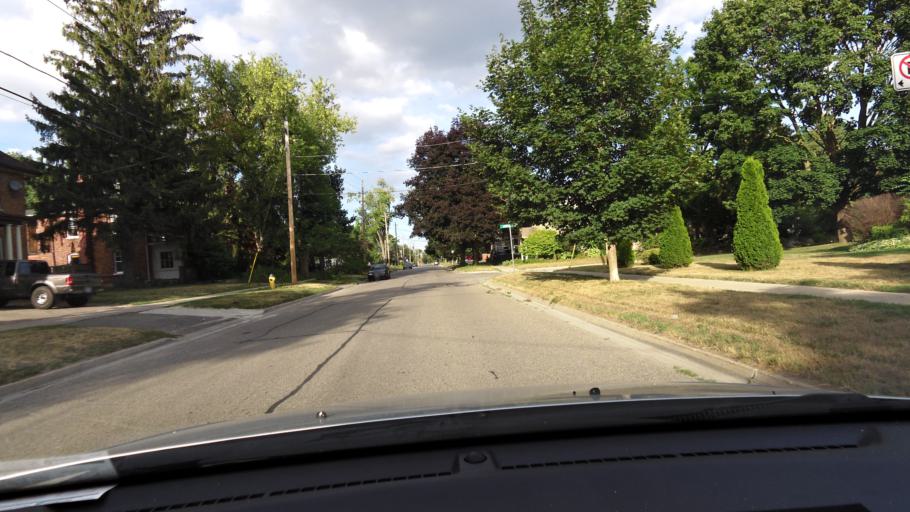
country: CA
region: Ontario
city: Angus
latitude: 44.1519
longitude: -79.8738
